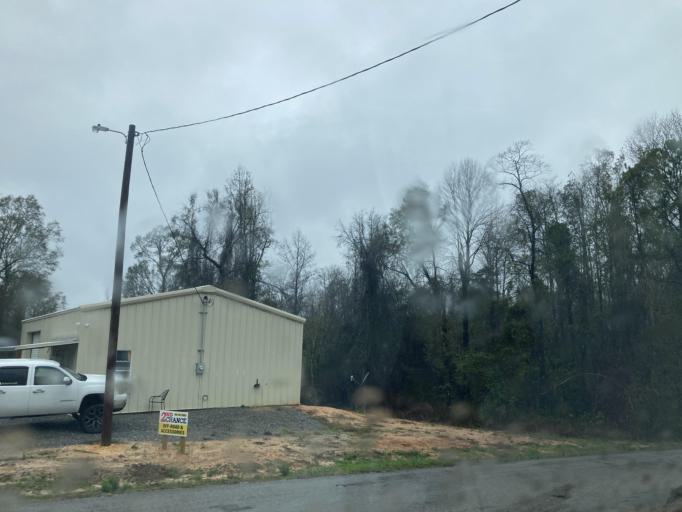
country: US
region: Mississippi
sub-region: Forrest County
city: Rawls Springs
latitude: 31.4403
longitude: -89.3509
